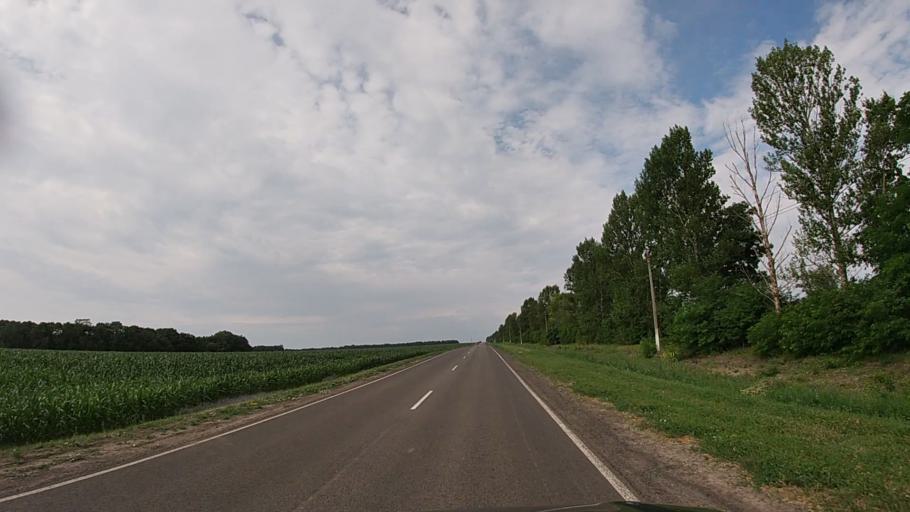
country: RU
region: Belgorod
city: Krasnaya Yaruga
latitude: 50.8285
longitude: 35.4745
